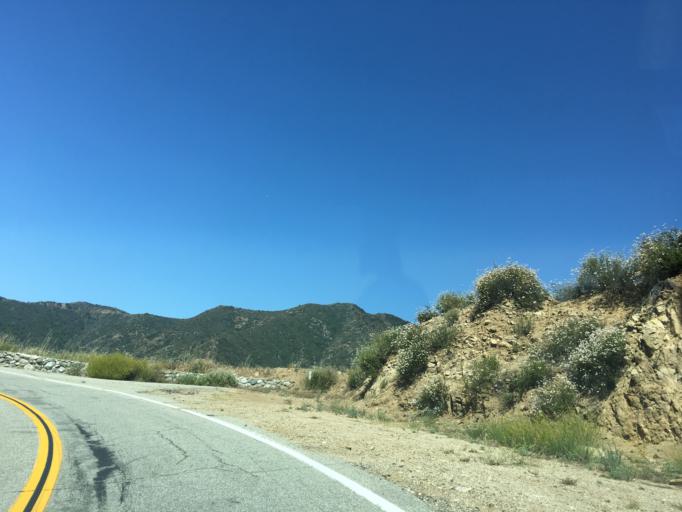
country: US
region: California
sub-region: Los Angeles County
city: Glendora
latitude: 34.2131
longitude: -117.8019
